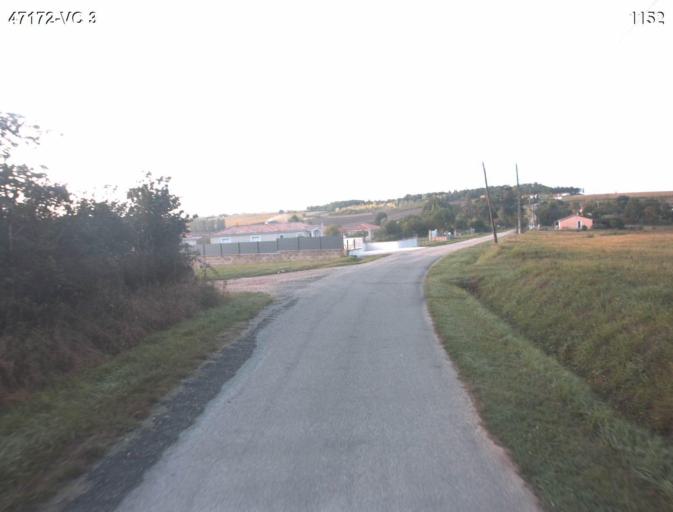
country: FR
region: Aquitaine
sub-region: Departement du Lot-et-Garonne
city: Sainte-Colombe-en-Bruilhois
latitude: 44.1602
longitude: 0.4961
